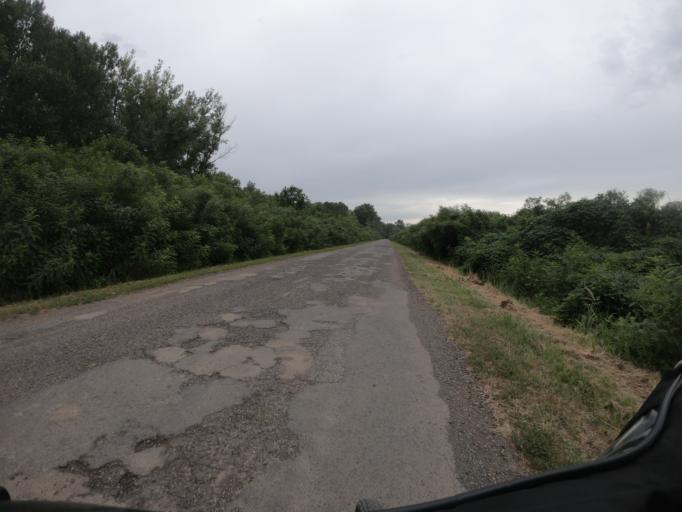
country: HU
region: Hajdu-Bihar
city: Tiszacsege
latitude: 47.7207
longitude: 20.9509
